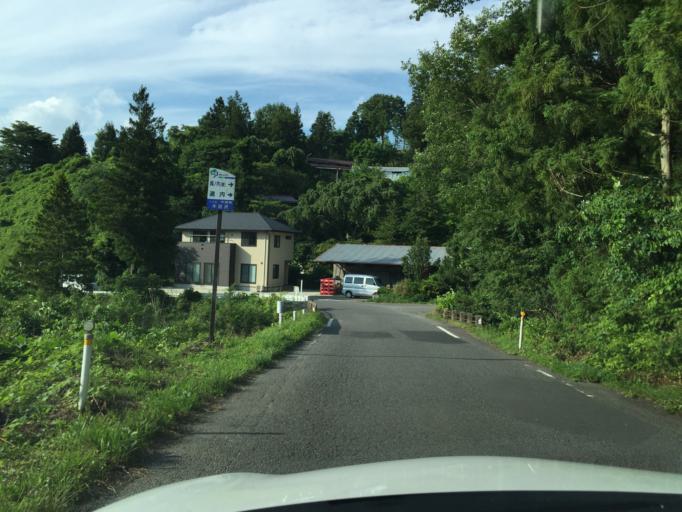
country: JP
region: Fukushima
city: Miharu
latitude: 37.3764
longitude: 140.5129
